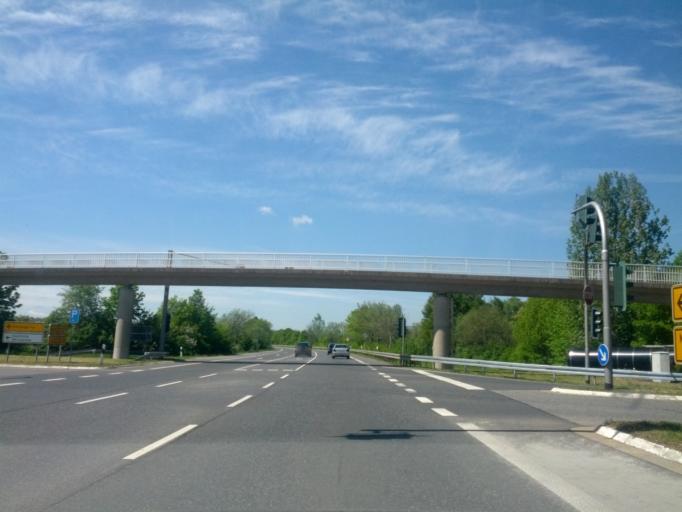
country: DE
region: Hesse
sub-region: Regierungsbezirk Kassel
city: Eschwege
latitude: 51.1983
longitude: 10.0594
